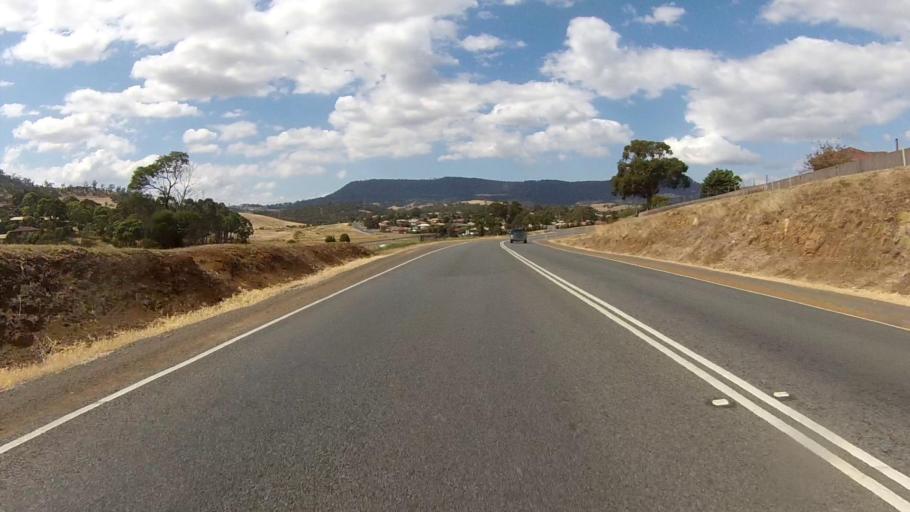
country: AU
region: Tasmania
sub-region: Glenorchy
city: Austins Ferry
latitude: -42.7473
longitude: 147.2667
